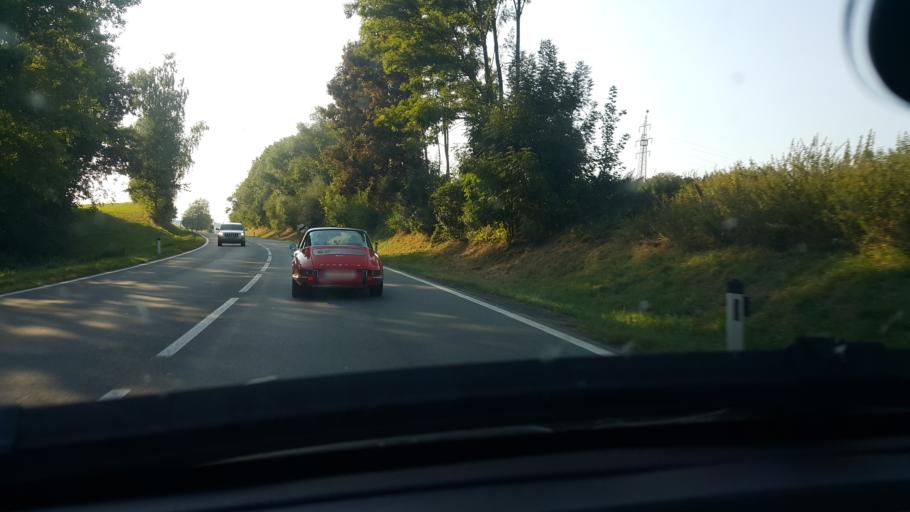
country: AT
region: Carinthia
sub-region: Politischer Bezirk Klagenfurt Land
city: Moosburg
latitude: 46.6723
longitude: 14.1608
